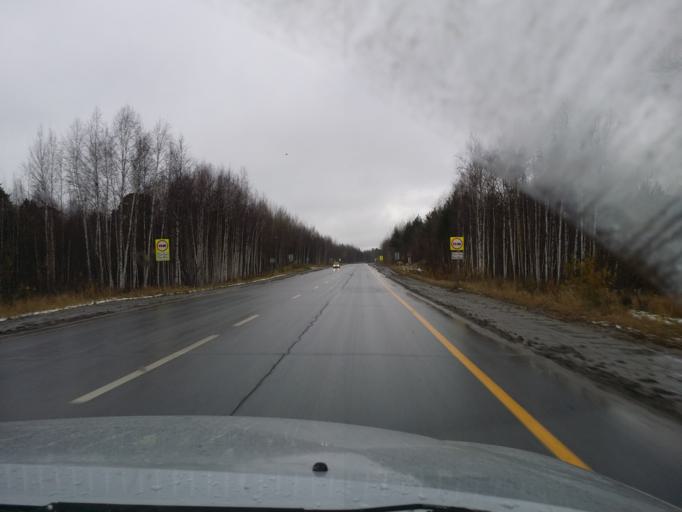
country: RU
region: Khanty-Mansiyskiy Avtonomnyy Okrug
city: Megion
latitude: 61.0985
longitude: 76.0615
